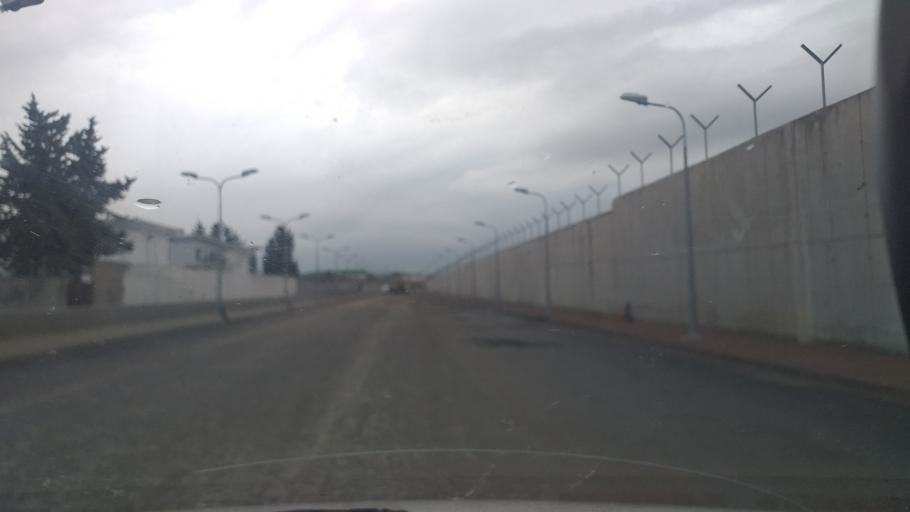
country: TN
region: Ariana
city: Ariana
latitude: 36.8542
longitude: 10.2127
